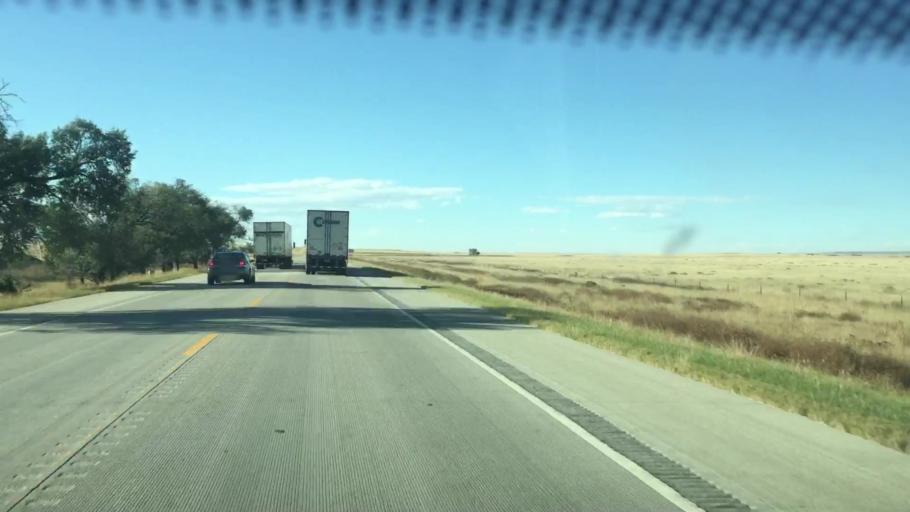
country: US
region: Colorado
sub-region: Lincoln County
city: Hugo
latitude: 38.9373
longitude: -103.2061
